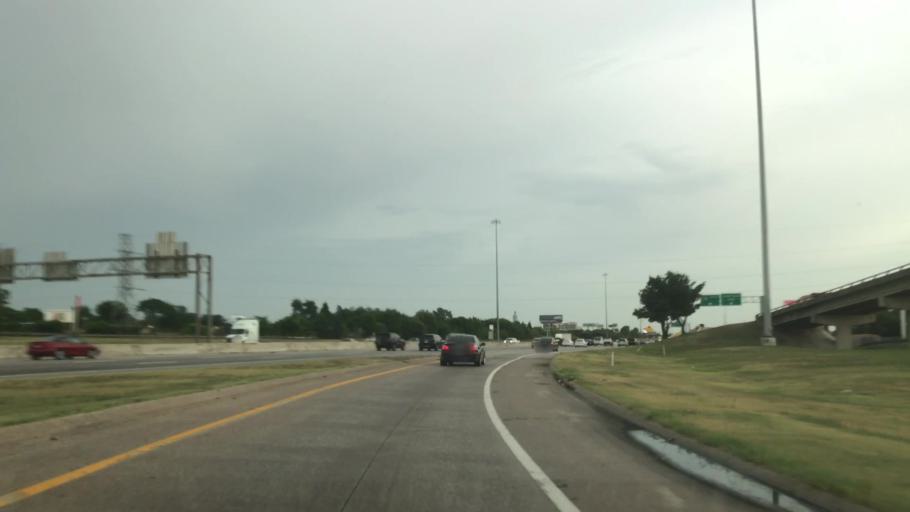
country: US
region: Texas
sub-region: Dallas County
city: Mesquite
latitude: 32.8212
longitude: -96.6297
